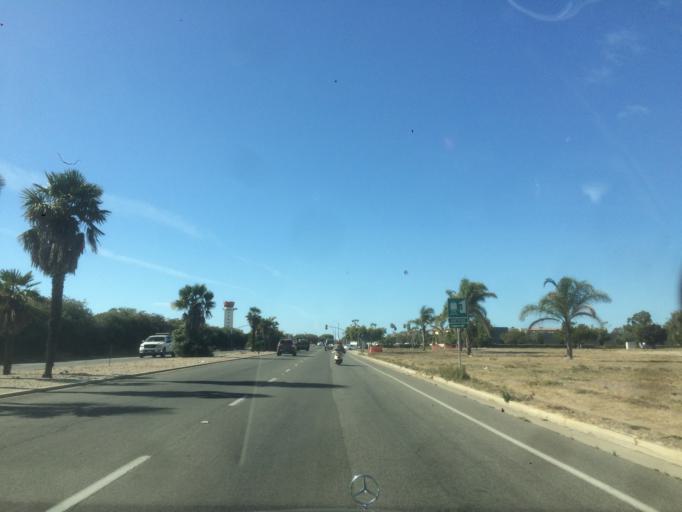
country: US
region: California
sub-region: Santa Barbara County
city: Goleta
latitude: 34.4334
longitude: -119.8395
